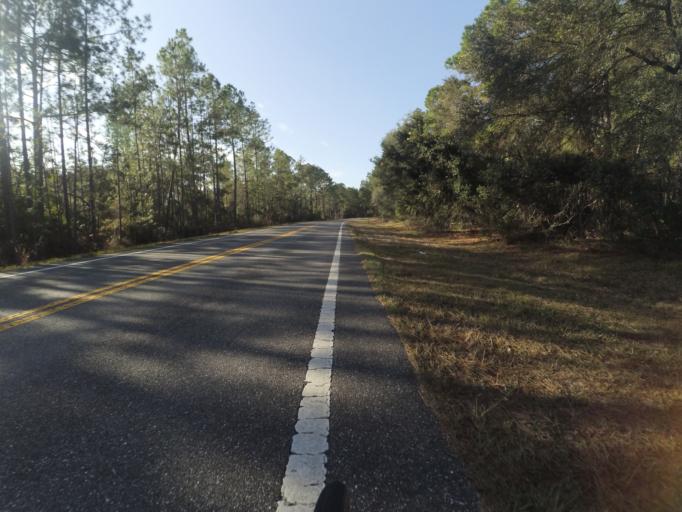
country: US
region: Florida
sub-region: Lake County
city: Astor
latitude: 29.1471
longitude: -81.5760
